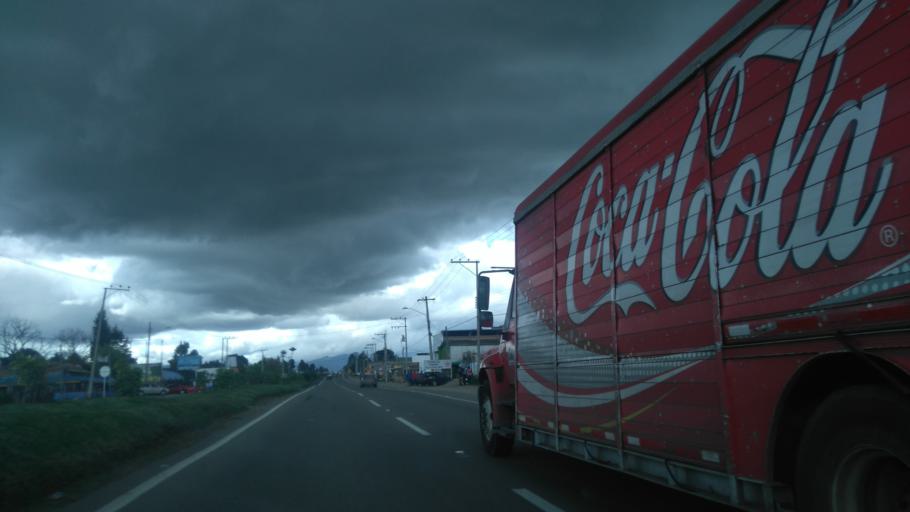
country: CO
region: Cundinamarca
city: El Rosal
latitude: 4.7962
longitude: -74.2061
